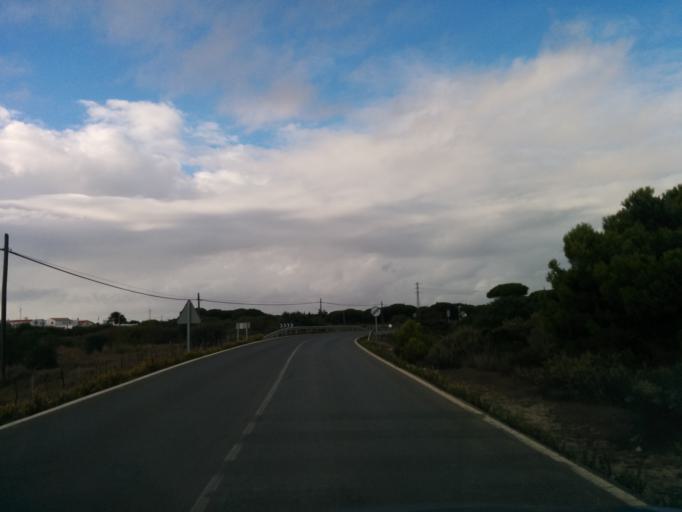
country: ES
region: Andalusia
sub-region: Provincia de Cadiz
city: Vejer de la Frontera
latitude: 36.1927
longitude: -6.0311
